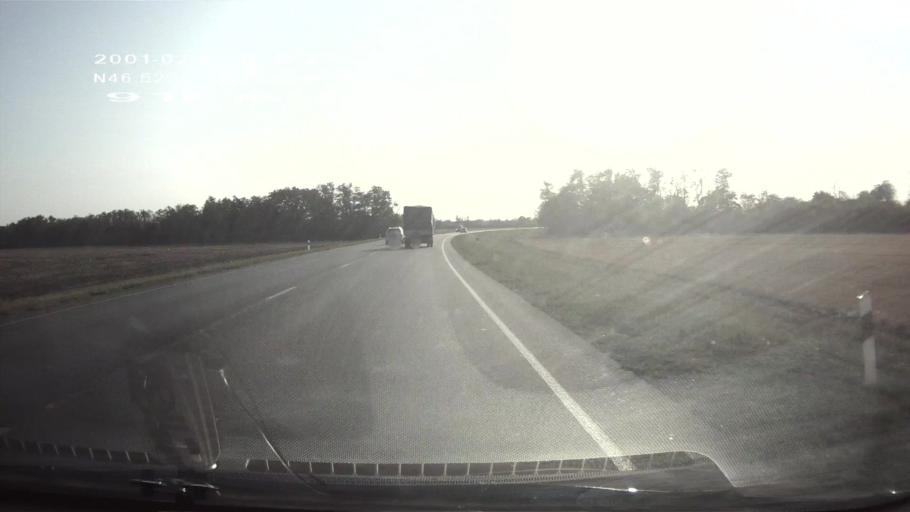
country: RU
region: Rostov
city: Tselina
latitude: 46.5243
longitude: 41.1616
